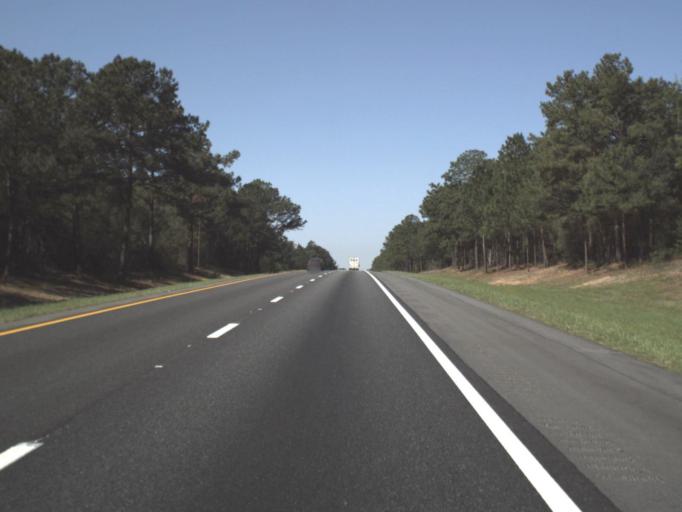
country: US
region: Florida
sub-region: Walton County
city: DeFuniak Springs
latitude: 30.6955
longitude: -85.9989
